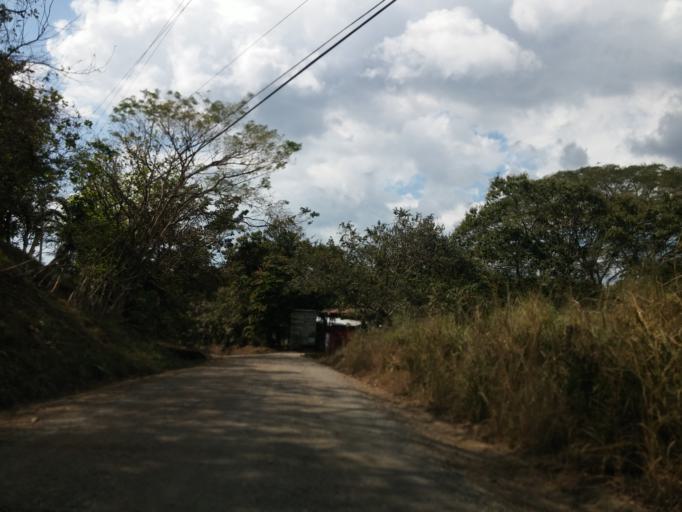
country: CR
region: Alajuela
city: Orotina
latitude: 9.9196
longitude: -84.5537
